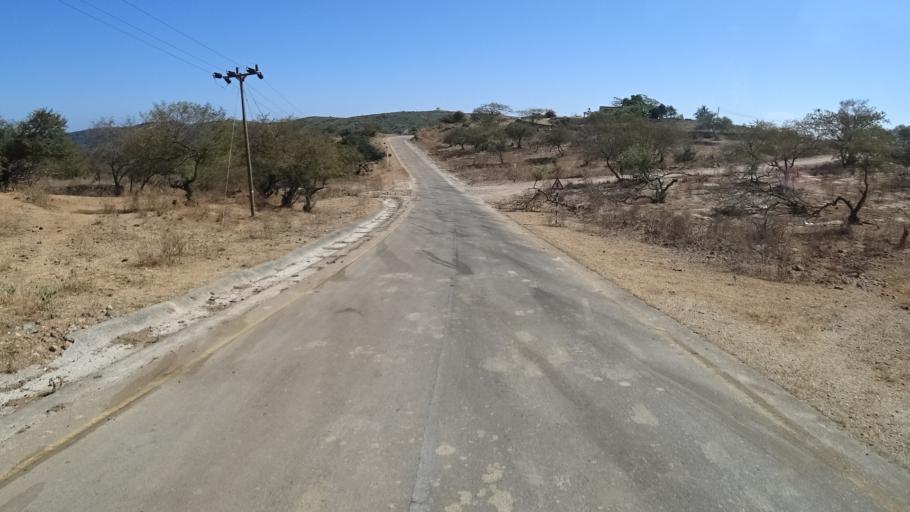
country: YE
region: Al Mahrah
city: Hawf
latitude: 16.7579
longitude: 53.3395
